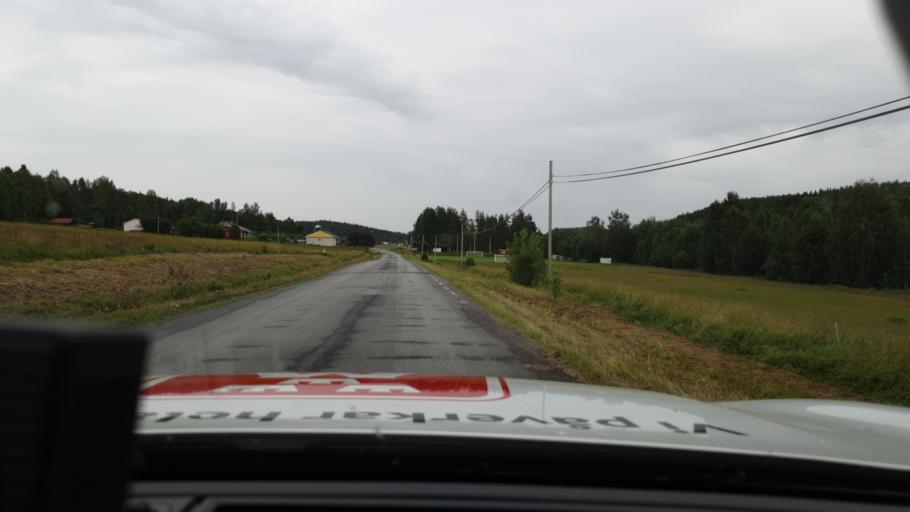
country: SE
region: Norrbotten
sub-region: Bodens Kommun
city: Saevast
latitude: 65.8740
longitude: 21.8801
